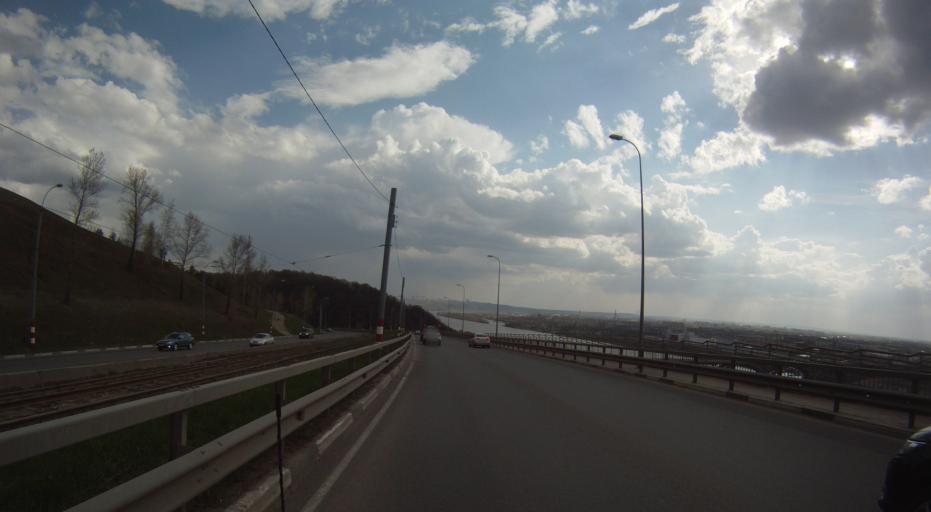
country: RU
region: Nizjnij Novgorod
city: Nizhniy Novgorod
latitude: 56.3024
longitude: 43.9710
